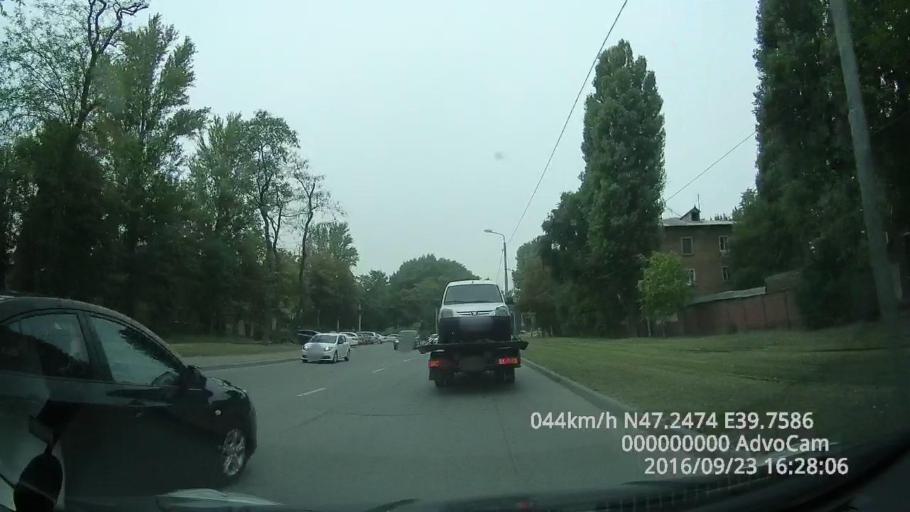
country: RU
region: Rostov
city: Imeni Chkalova
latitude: 47.2472
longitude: 39.7585
